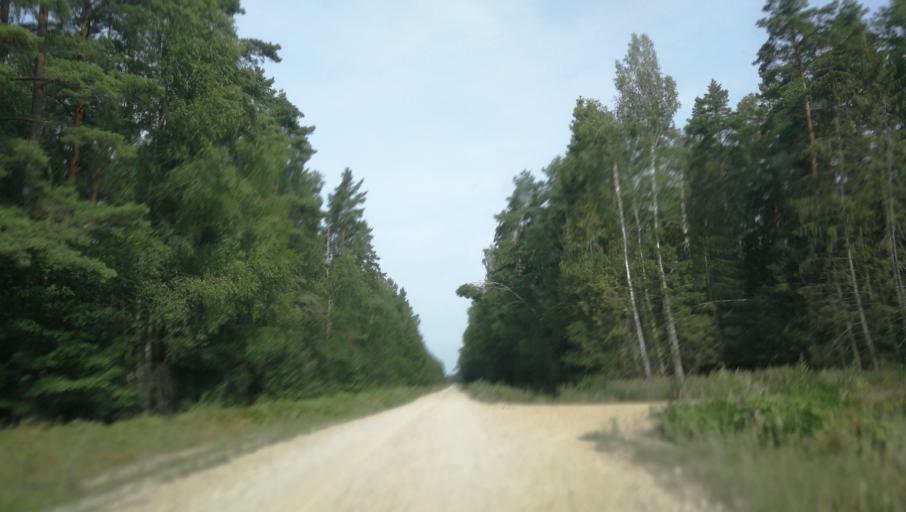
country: LV
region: Pavilostas
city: Pavilosta
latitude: 56.7841
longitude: 21.3506
